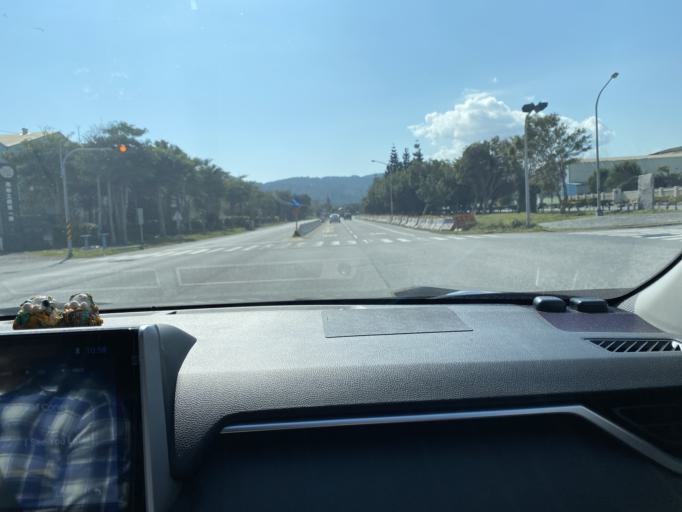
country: TW
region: Taiwan
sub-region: Hualien
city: Hualian
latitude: 23.9341
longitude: 121.5945
